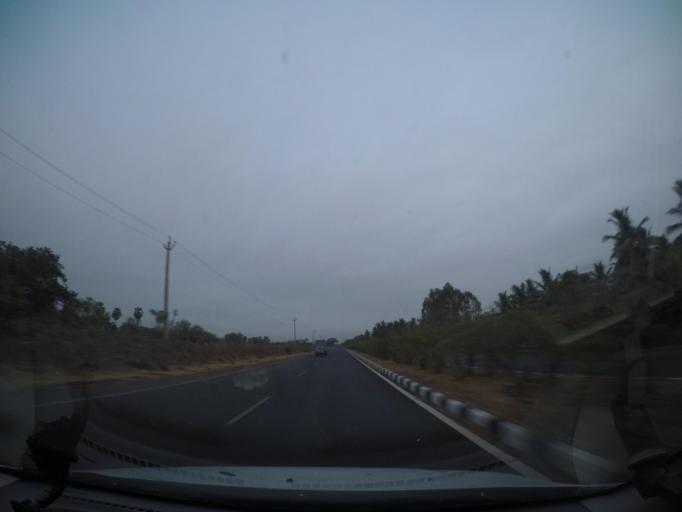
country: IN
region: Andhra Pradesh
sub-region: West Godavari
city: Tadepallegudem
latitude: 16.8074
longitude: 81.3147
